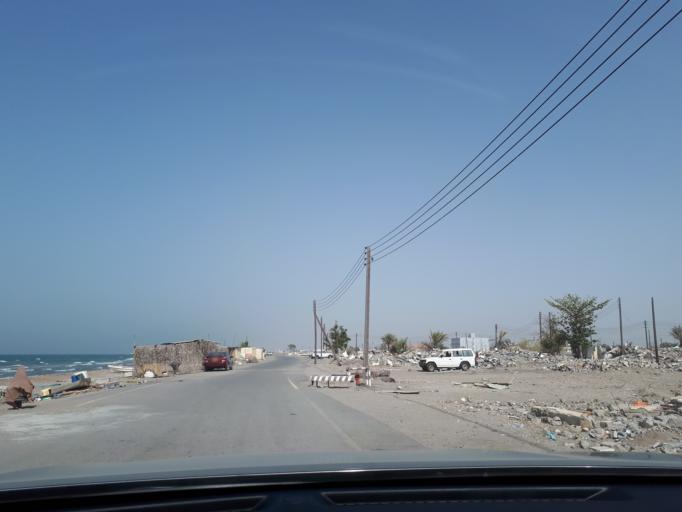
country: OM
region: Al Batinah
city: Barka'
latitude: 23.7089
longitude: 57.9060
